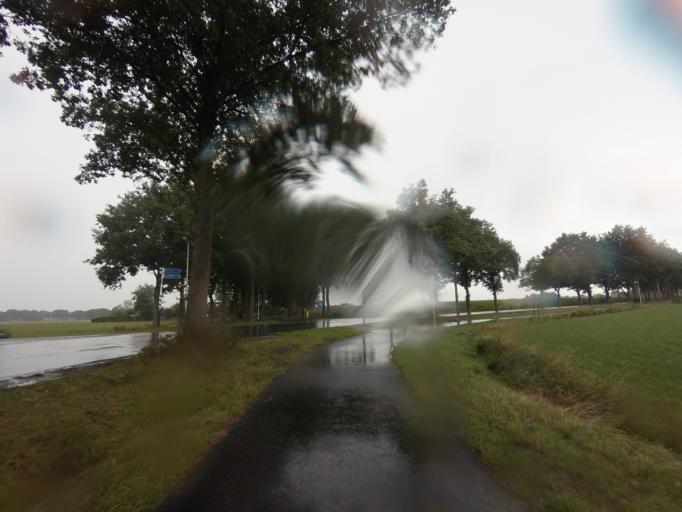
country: NL
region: Drenthe
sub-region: Gemeente Hoogeveen
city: Hoogeveen
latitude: 52.6683
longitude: 6.4935
